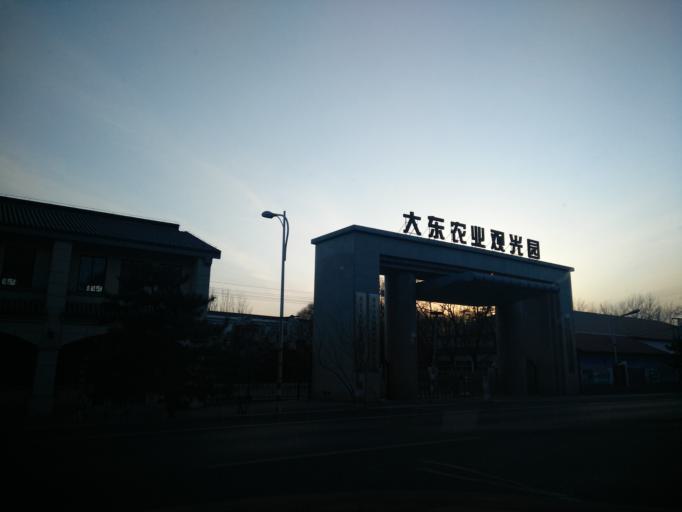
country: CN
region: Beijing
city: Qingyundian
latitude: 39.6721
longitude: 116.5245
